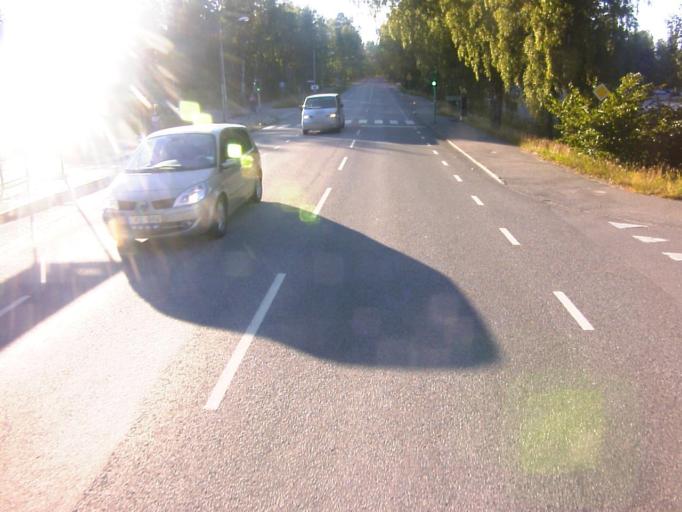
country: SE
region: Soedermanland
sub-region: Eskilstuna Kommun
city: Hallbybrunn
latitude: 59.3939
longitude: 16.4216
